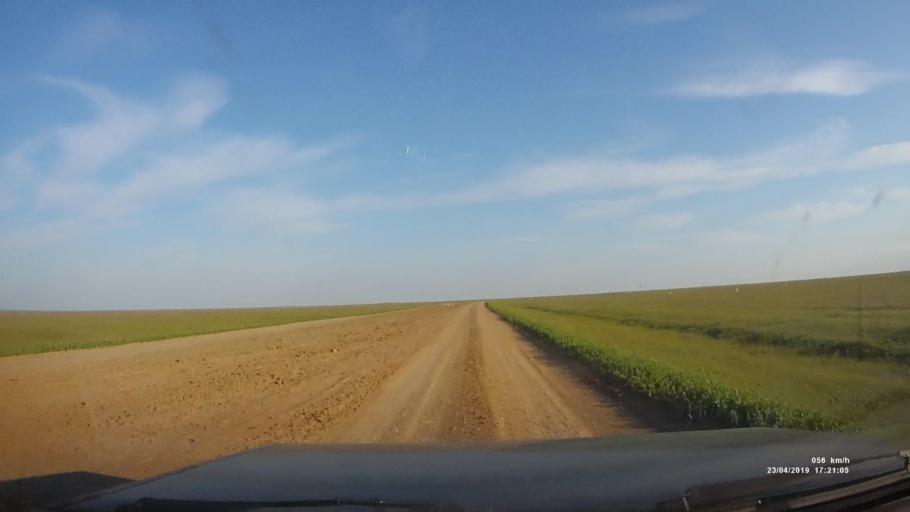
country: RU
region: Kalmykiya
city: Priyutnoye
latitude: 46.1788
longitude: 43.5037
